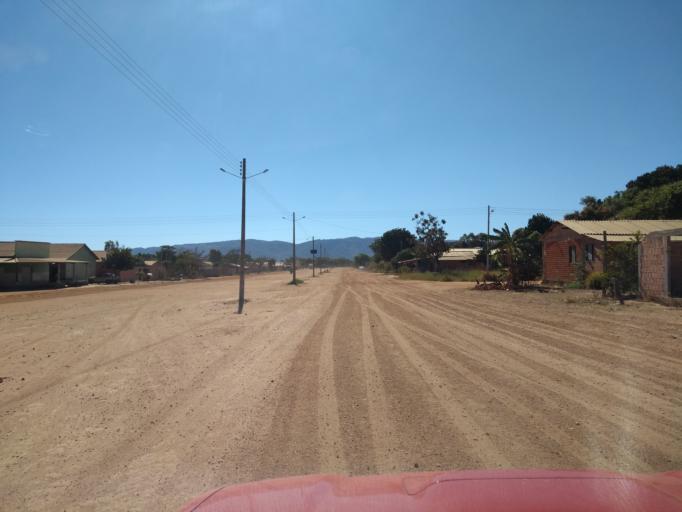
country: BR
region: Goias
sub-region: Cavalcante
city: Cavalcante
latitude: -13.7993
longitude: -47.4448
